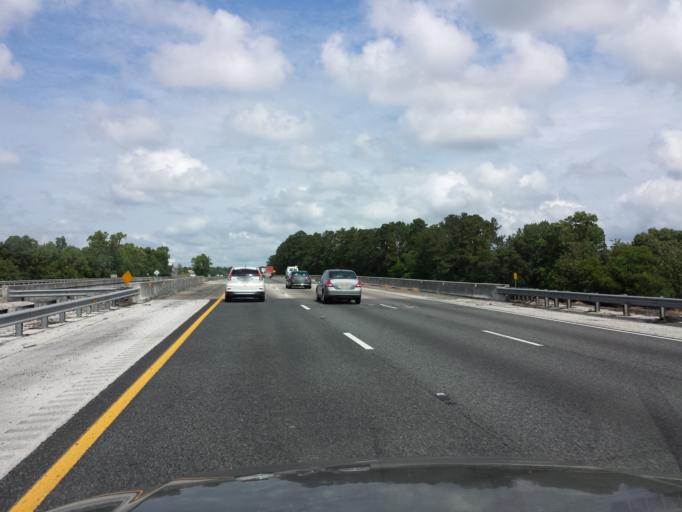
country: US
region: Florida
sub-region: Marion County
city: Citra
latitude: 29.4066
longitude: -82.2473
